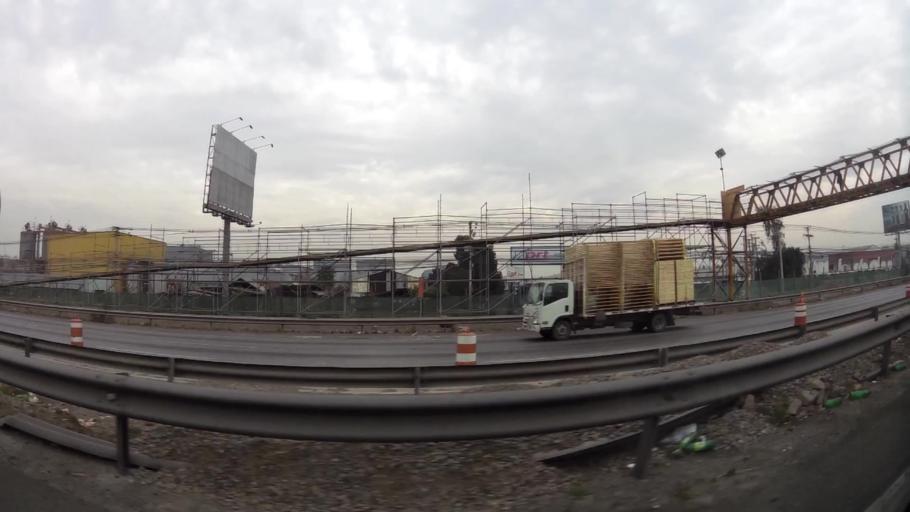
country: CL
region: Santiago Metropolitan
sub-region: Provincia de Chacabuco
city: Chicureo Abajo
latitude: -33.3398
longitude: -70.7117
